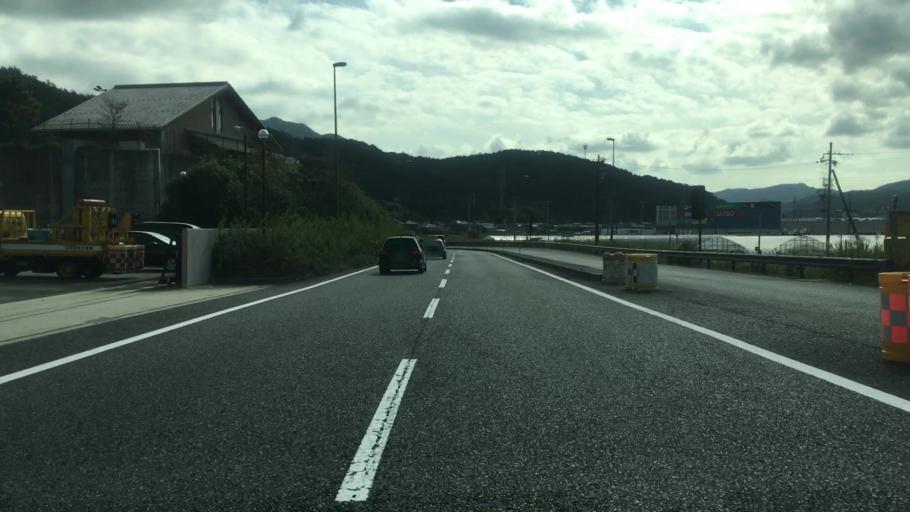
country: JP
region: Kyoto
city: Fukuchiyama
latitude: 35.1612
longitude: 135.0457
